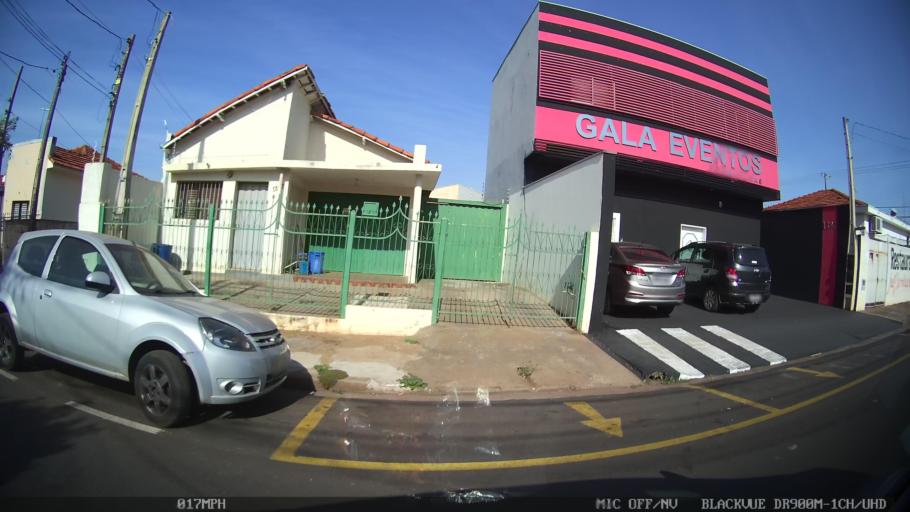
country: BR
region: Sao Paulo
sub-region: Sao Jose Do Rio Preto
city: Sao Jose do Rio Preto
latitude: -20.8018
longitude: -49.3882
